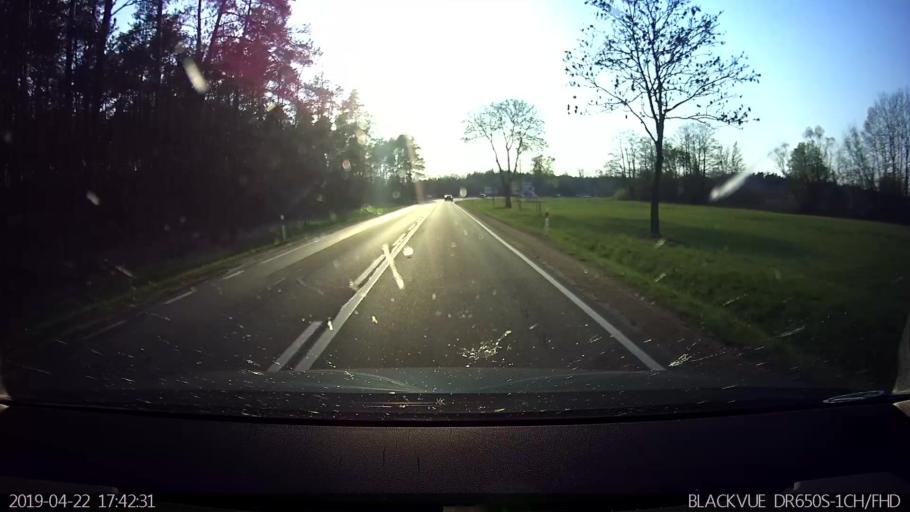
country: PL
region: Masovian Voivodeship
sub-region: Powiat wegrowski
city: Wegrow
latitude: 52.4042
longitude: 22.0766
